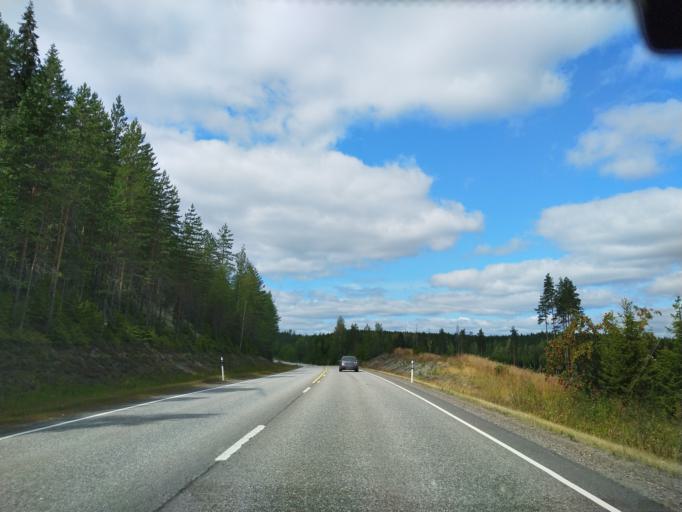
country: FI
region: Haeme
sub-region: Riihimaeki
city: Loppi
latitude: 60.7364
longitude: 24.3793
